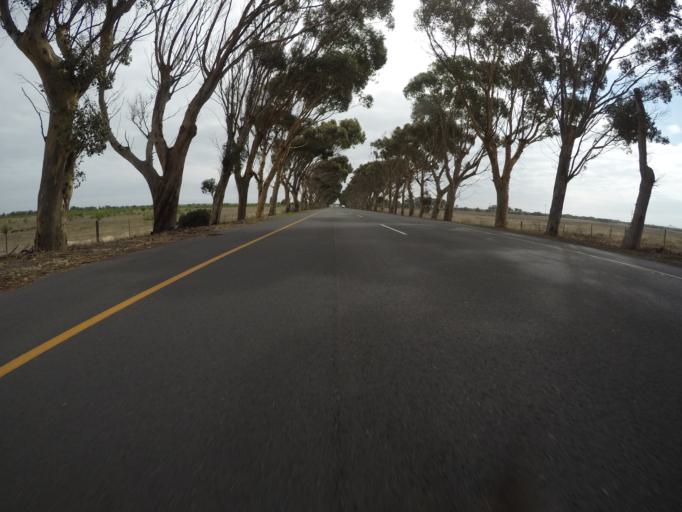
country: ZA
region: Western Cape
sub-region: City of Cape Town
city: Sunset Beach
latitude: -33.7254
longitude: 18.4661
